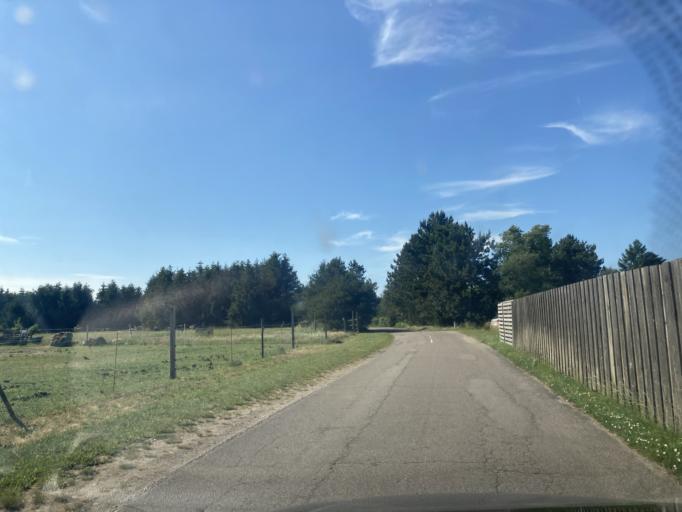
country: DK
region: Capital Region
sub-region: Halsnaes Kommune
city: Liseleje
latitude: 56.0038
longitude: 11.9777
